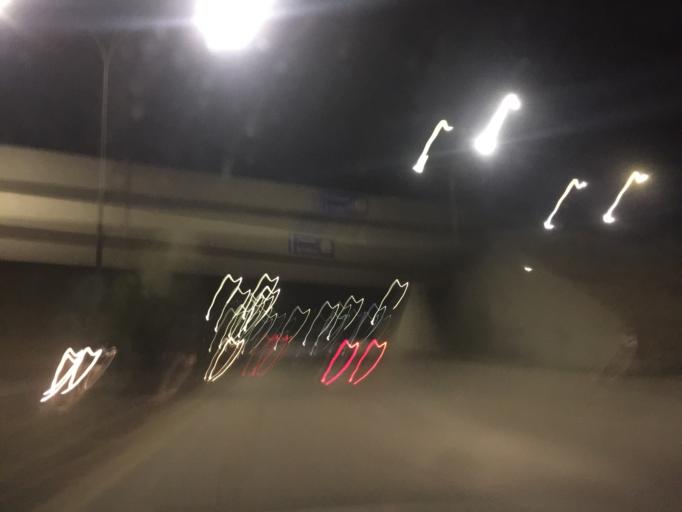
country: JO
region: Zarqa
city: Russeifa
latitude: 32.0246
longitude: 35.9820
